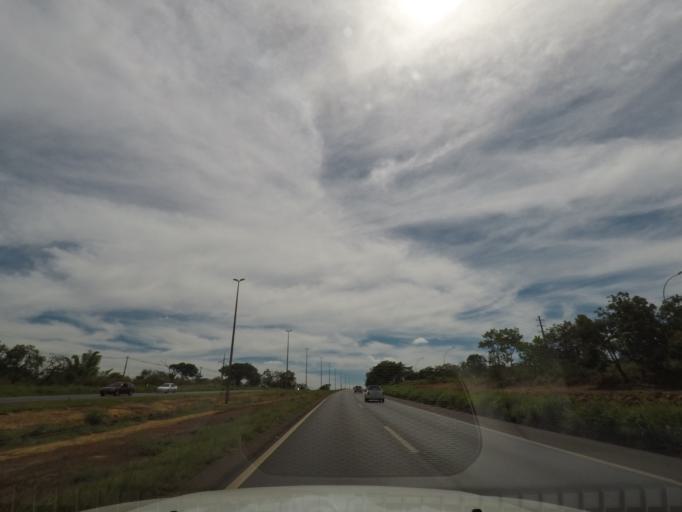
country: BR
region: Goias
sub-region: Planaltina
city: Planaltina
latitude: -15.5948
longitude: -47.6653
